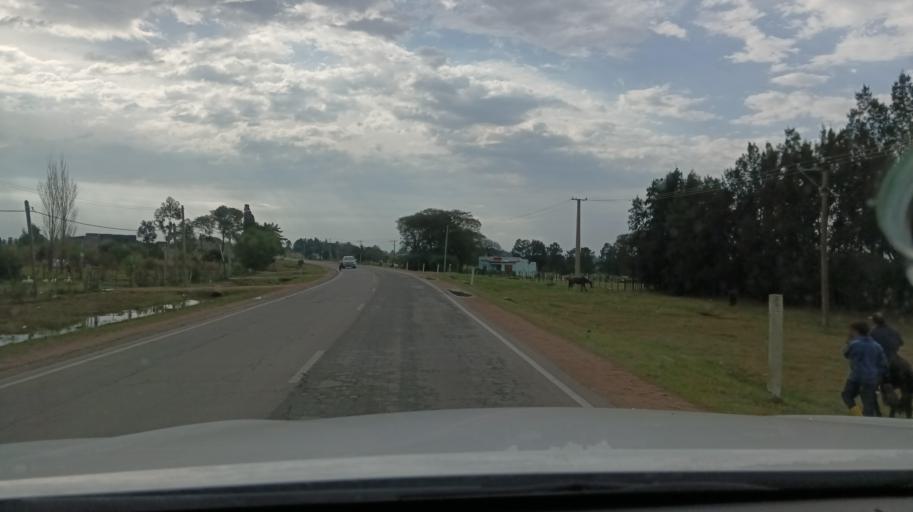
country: UY
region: Canelones
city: Toledo
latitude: -34.7285
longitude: -56.1132
